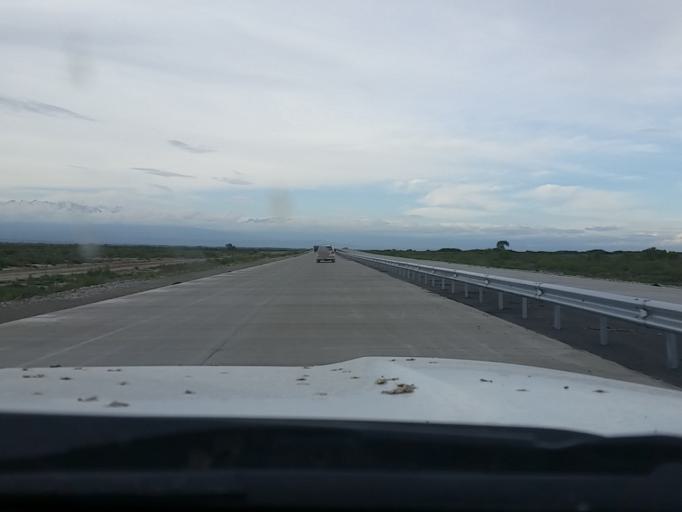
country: KZ
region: Almaty Oblysy
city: Zharkent
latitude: 44.0778
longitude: 80.0415
